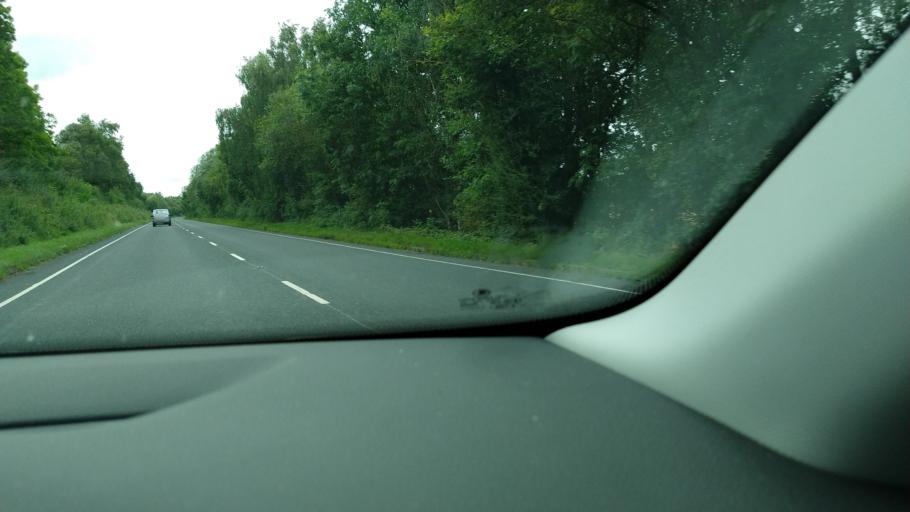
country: GB
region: England
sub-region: East Riding of Yorkshire
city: Barmby on the Marsh
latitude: 53.7224
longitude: -0.9810
